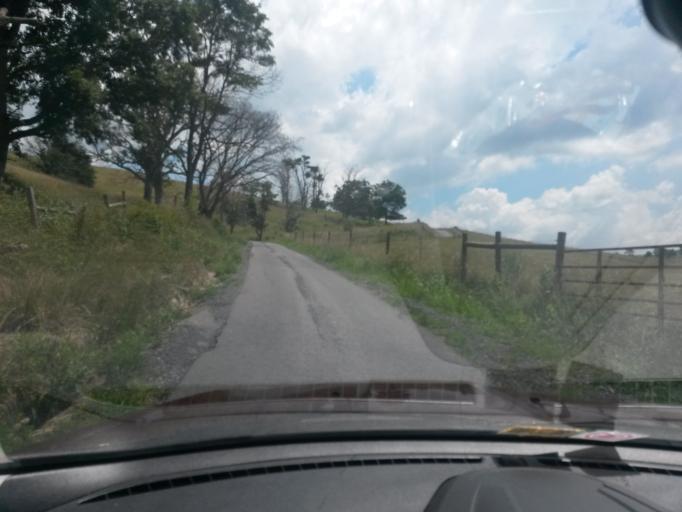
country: US
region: West Virginia
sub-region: Monroe County
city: Union
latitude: 37.5564
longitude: -80.5175
